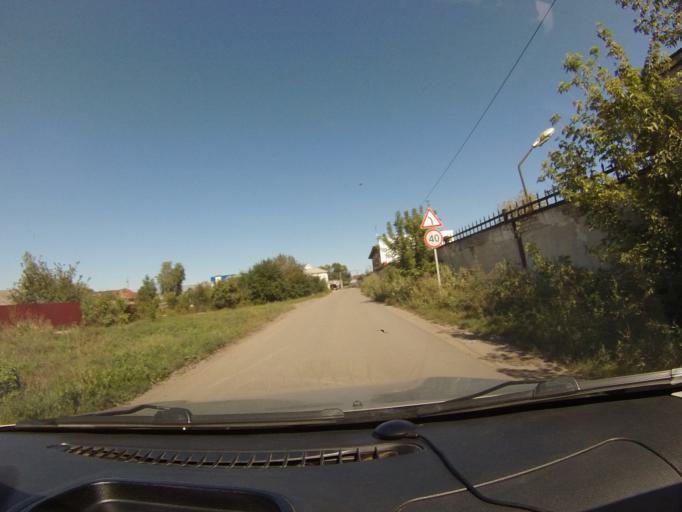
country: RU
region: Tambov
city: Donskoye
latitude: 52.7596
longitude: 41.4659
